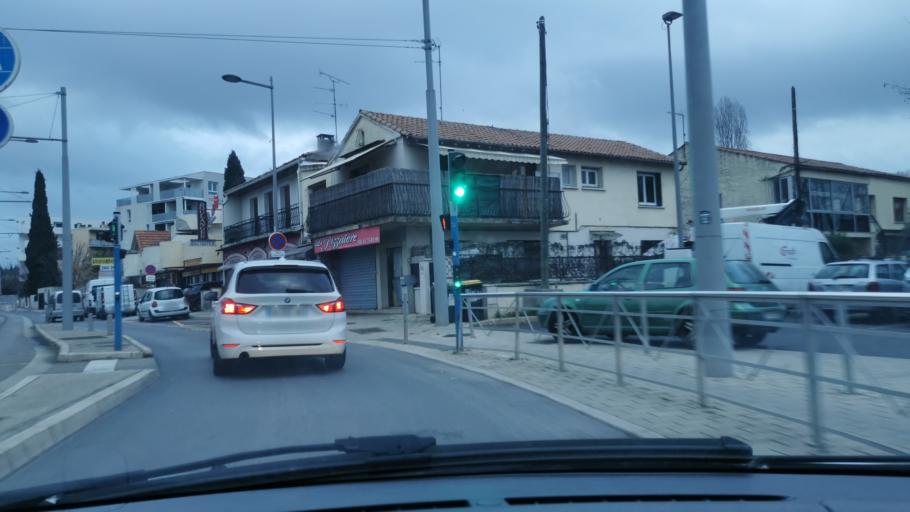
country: FR
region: Languedoc-Roussillon
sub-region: Departement de l'Herault
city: Montpellier
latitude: 43.5930
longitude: 3.8749
